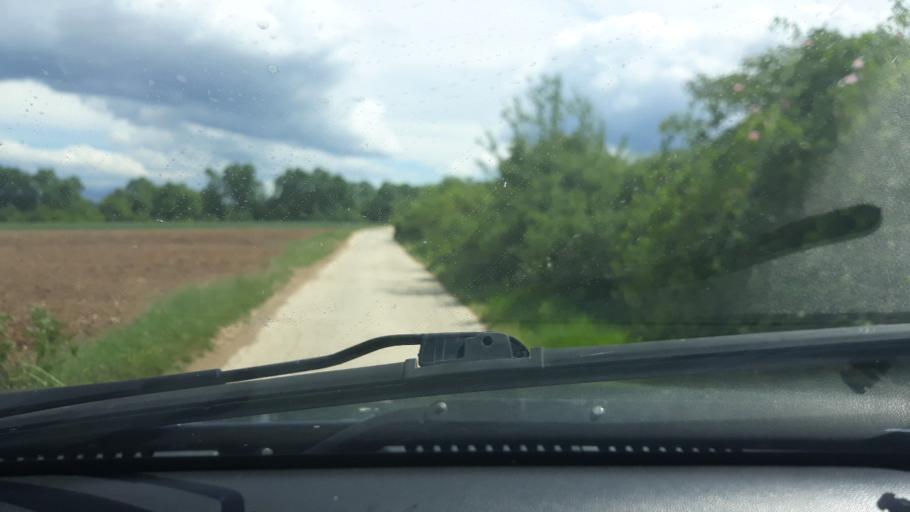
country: MK
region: Krivogastani
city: Krivogashtani
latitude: 41.3326
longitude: 21.3022
